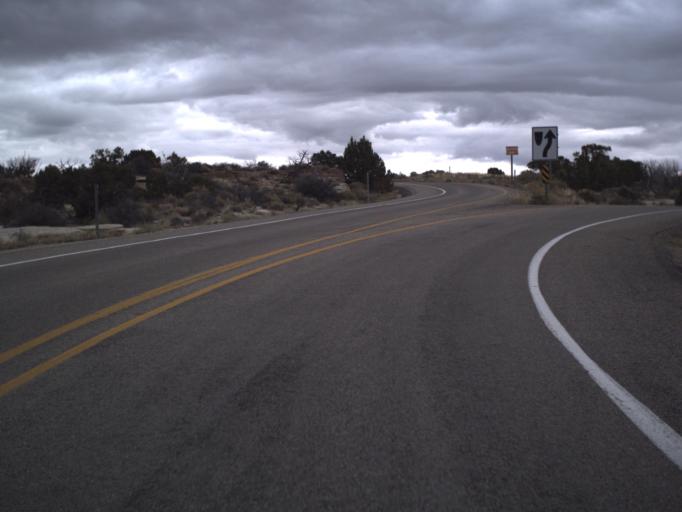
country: US
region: Utah
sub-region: Emery County
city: Ferron
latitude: 38.8293
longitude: -111.1177
